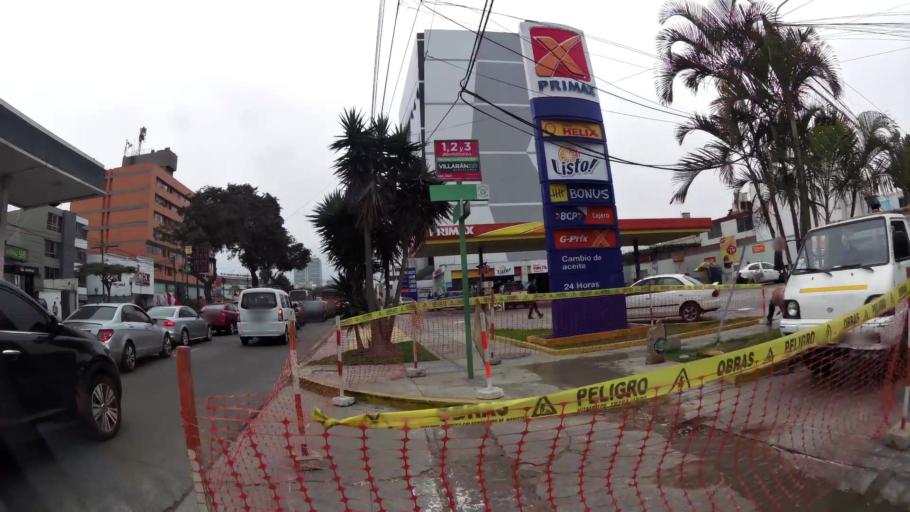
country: PE
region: Lima
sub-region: Lima
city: Surco
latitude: -12.1276
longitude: -77.0106
